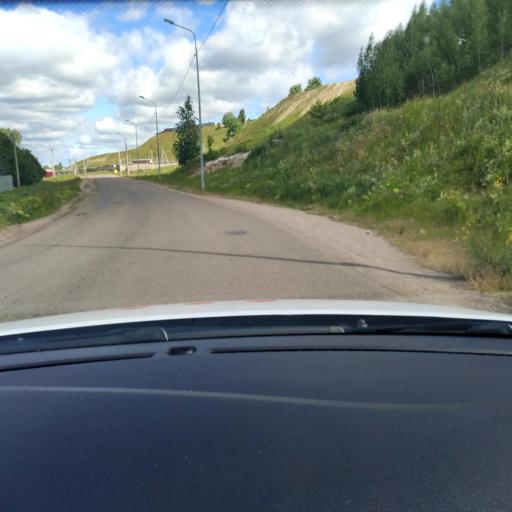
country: RU
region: Tatarstan
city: Vysokaya Gora
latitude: 55.8554
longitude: 49.2458
